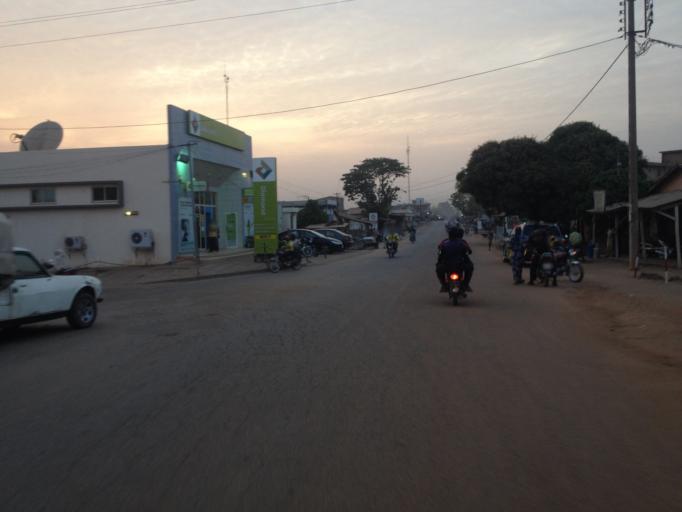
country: BJ
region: Borgou
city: Parakou
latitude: 9.3413
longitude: 2.6259
